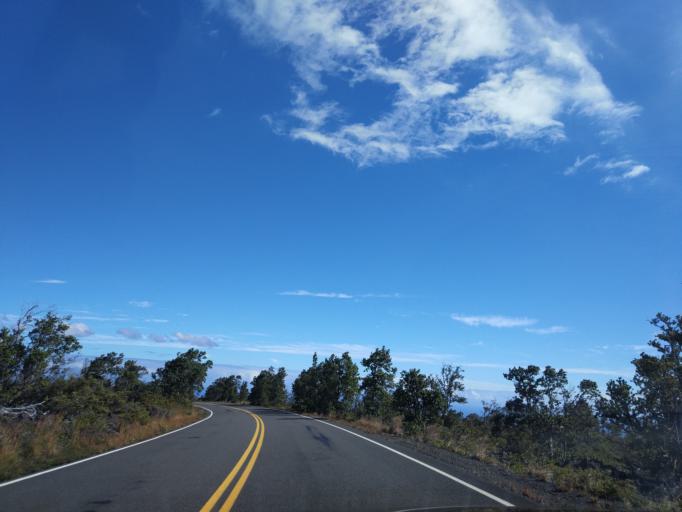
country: US
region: Hawaii
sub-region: Hawaii County
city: Volcano
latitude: 19.3382
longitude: -155.2076
